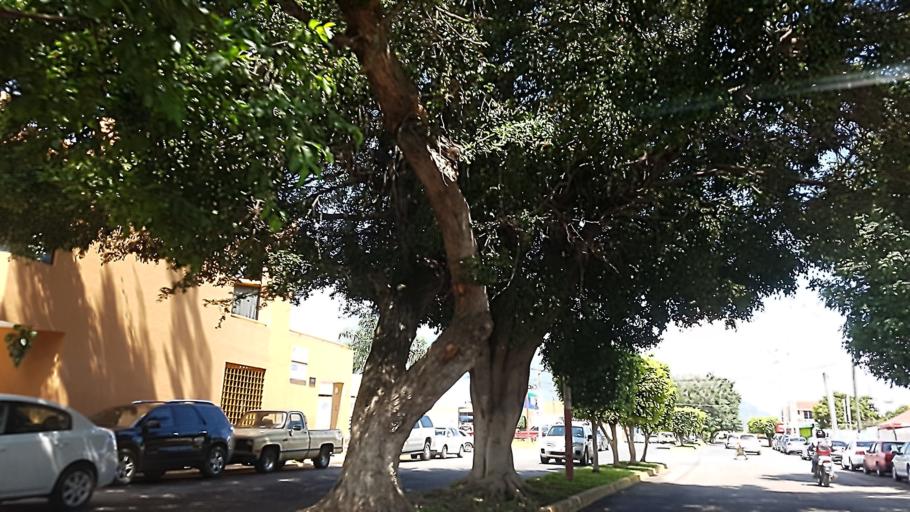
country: MX
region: Nayarit
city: Tepic
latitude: 21.4847
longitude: -104.8818
